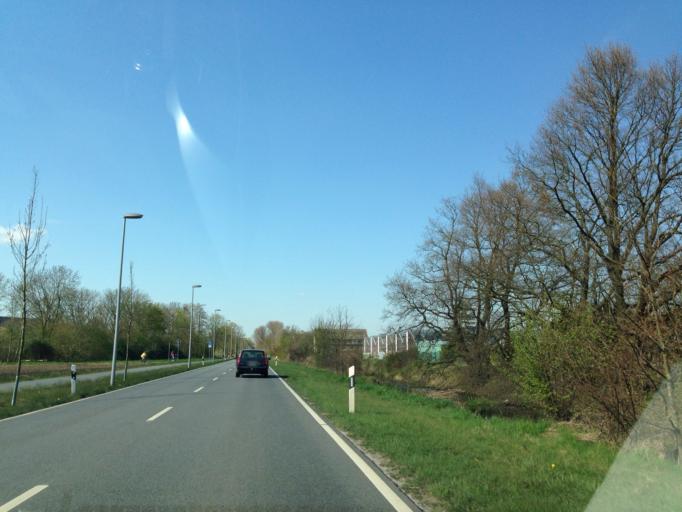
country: DE
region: North Rhine-Westphalia
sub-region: Regierungsbezirk Munster
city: Muenster
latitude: 51.9883
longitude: 7.6259
